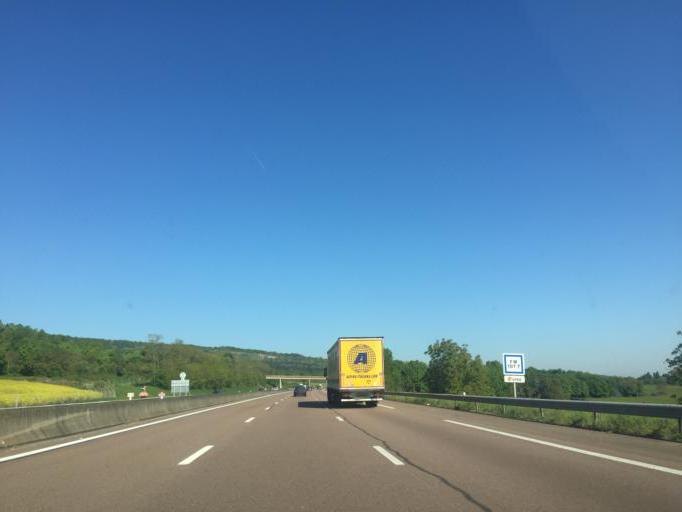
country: FR
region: Bourgogne
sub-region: Departement de Saone-et-Loire
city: Sennecey-le-Grand
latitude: 46.6147
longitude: 4.8687
